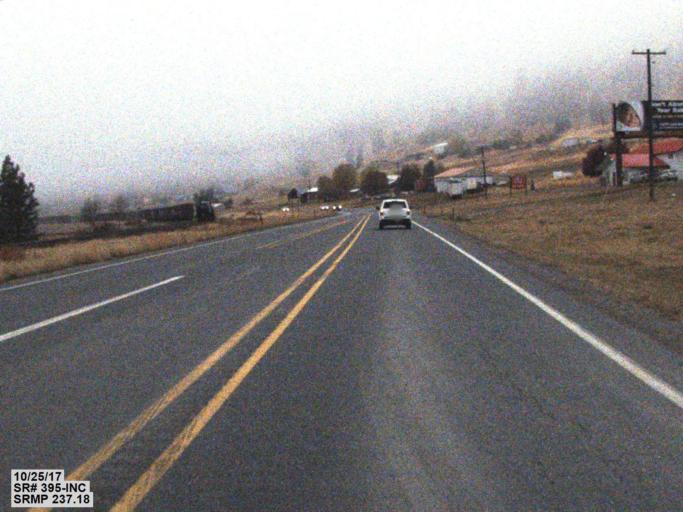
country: US
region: Washington
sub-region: Stevens County
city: Kettle Falls
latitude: 48.6093
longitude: -118.0347
